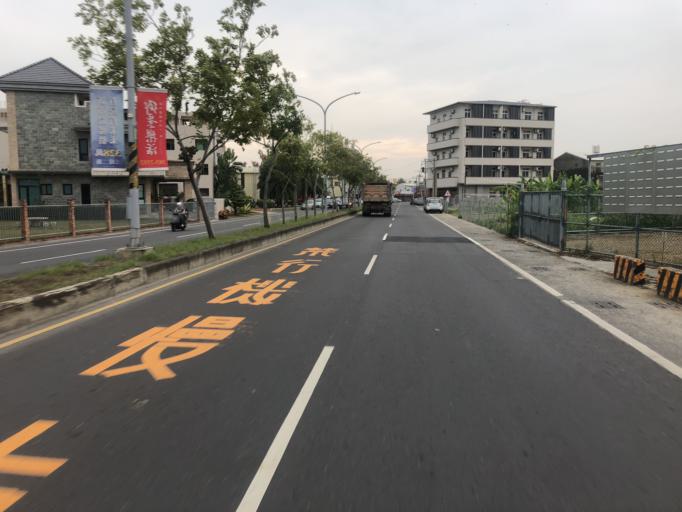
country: TW
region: Taiwan
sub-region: Tainan
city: Tainan
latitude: 23.1356
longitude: 120.2855
